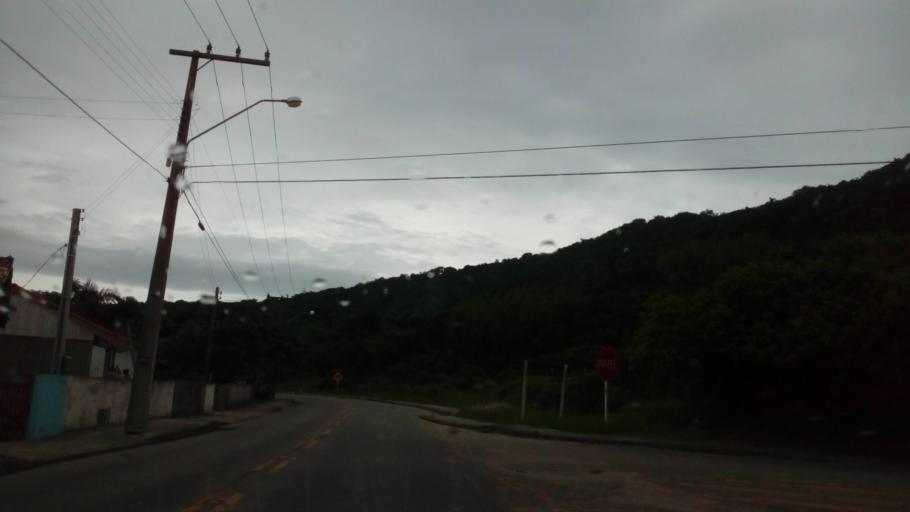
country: BR
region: Santa Catarina
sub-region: Laguna
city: Laguna
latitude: -28.5165
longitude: -48.7705
